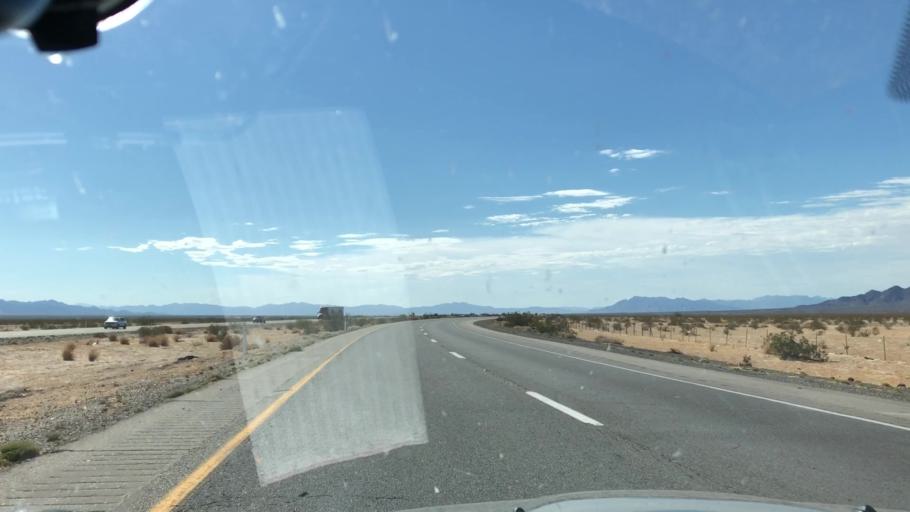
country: US
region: California
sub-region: Riverside County
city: Mesa Verde
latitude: 33.6313
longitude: -115.0747
